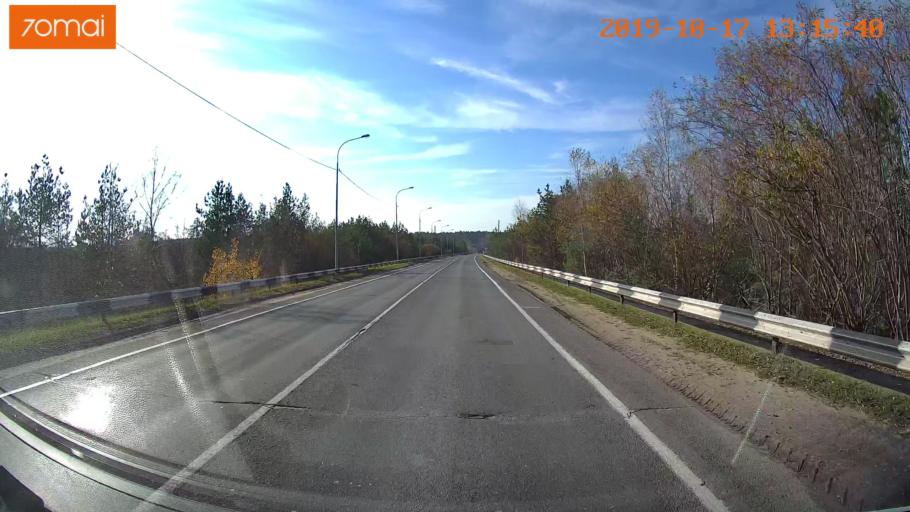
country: RU
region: Rjazan
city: Gus'-Zheleznyy
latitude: 55.0524
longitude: 41.1566
